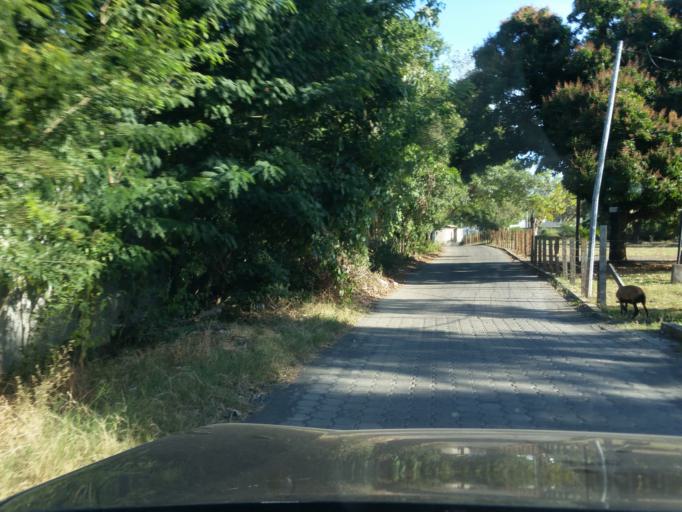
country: NI
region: Masaya
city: Ticuantepe
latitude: 12.0733
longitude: -86.2263
